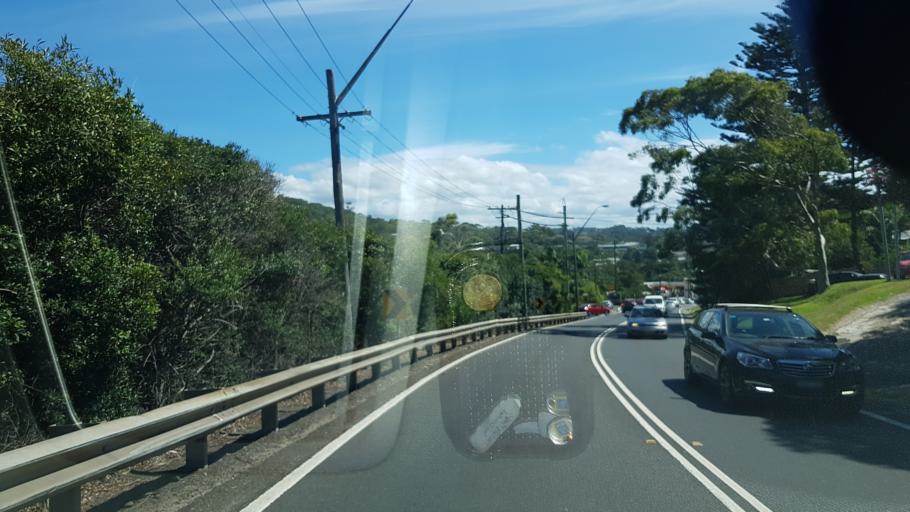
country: AU
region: New South Wales
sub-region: Pittwater
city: Bilgola Beach
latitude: -33.6424
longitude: 151.3294
